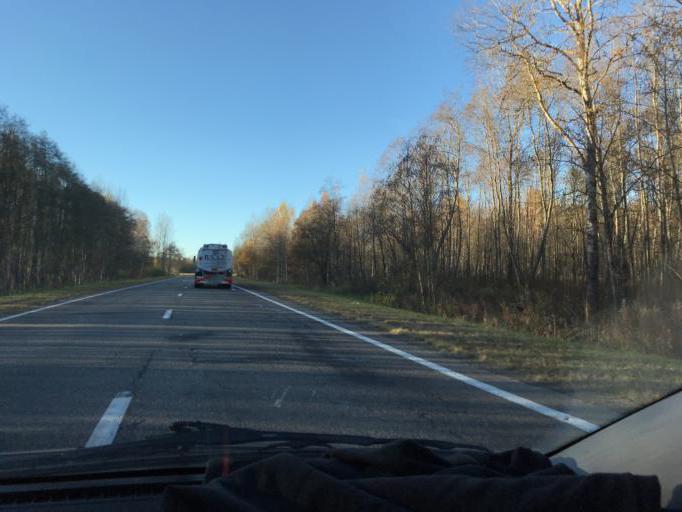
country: BY
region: Vitebsk
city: Vitebsk
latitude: 55.3592
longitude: 30.1747
